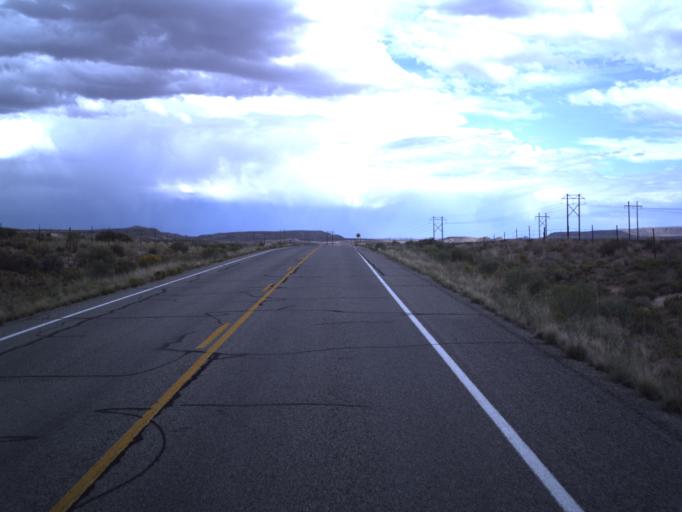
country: US
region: Utah
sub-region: San Juan County
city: Blanding
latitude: 37.3002
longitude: -109.4363
